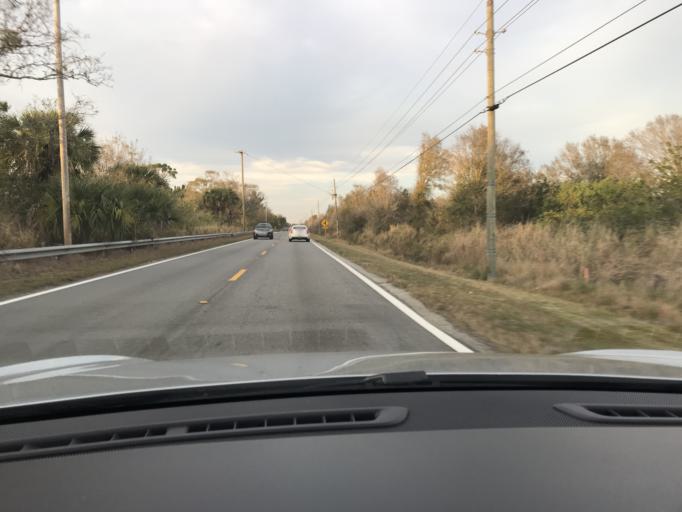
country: US
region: Florida
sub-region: Saint Lucie County
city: Lakewood Park
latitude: 27.5359
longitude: -80.4311
